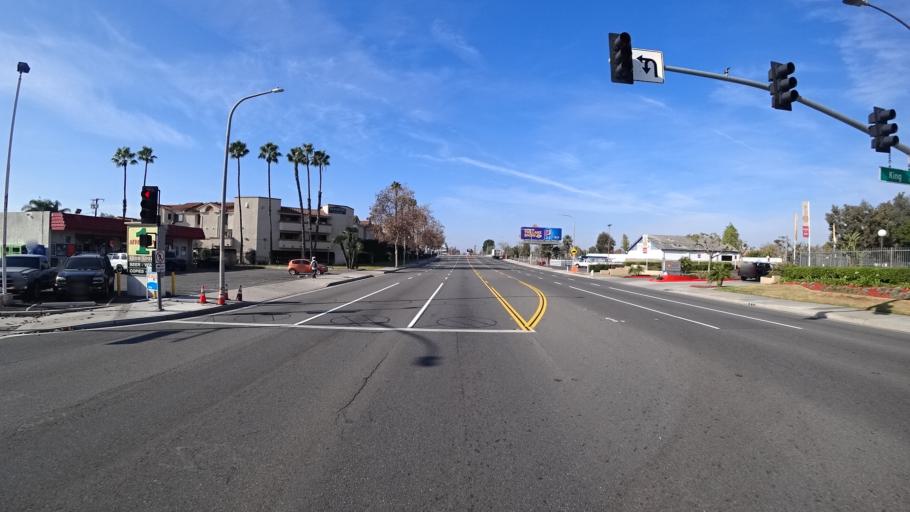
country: US
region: California
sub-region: Orange County
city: Santa Ana
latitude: 33.7599
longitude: -117.8981
